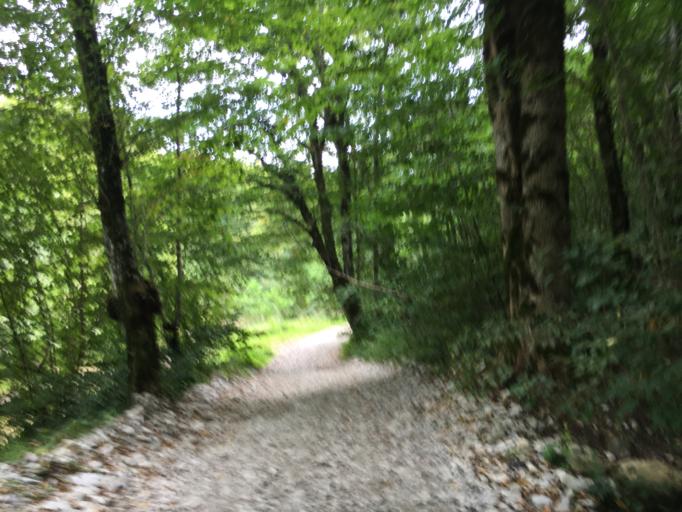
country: RU
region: Krasnodarskiy
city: Tuapse
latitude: 44.2613
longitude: 39.2156
